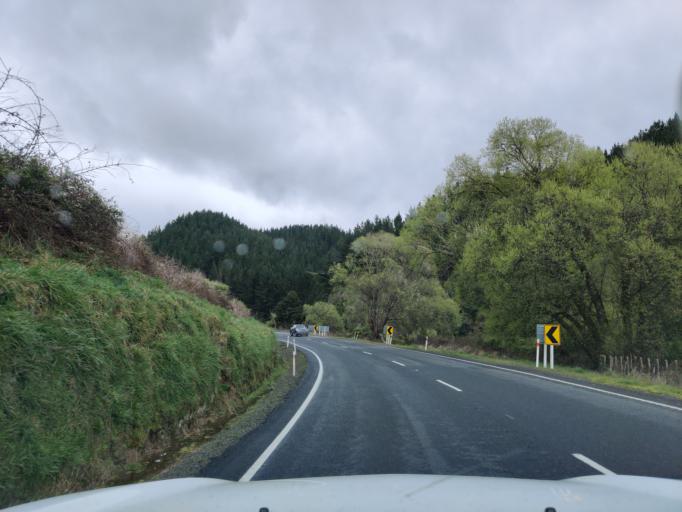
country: NZ
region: Waikato
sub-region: Otorohanga District
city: Otorohanga
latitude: -38.6508
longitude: 175.2082
